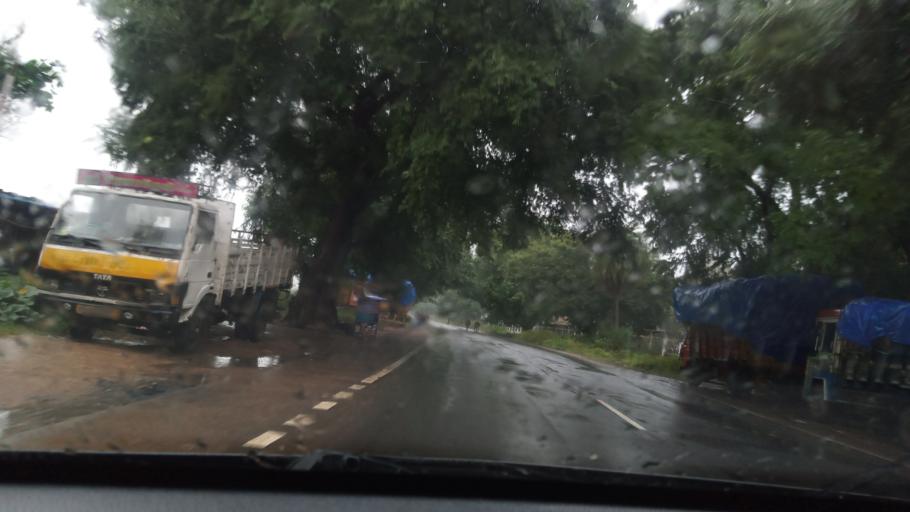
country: IN
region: Tamil Nadu
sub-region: Vellore
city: Kalavai
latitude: 12.8043
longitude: 79.4282
